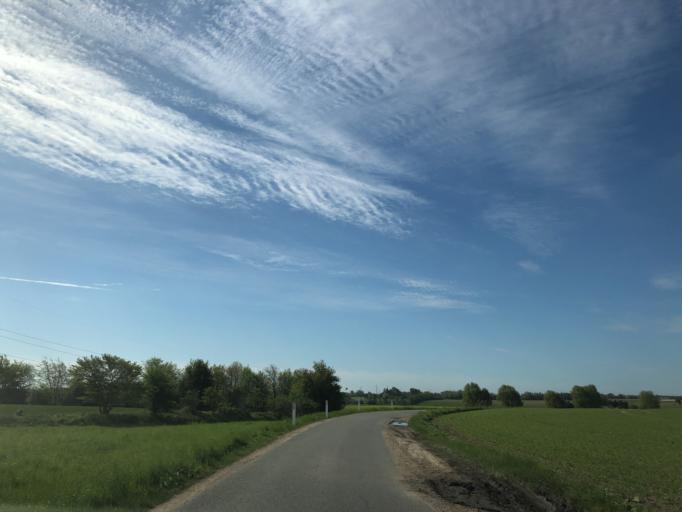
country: DK
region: Zealand
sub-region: Slagelse Kommune
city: Forlev
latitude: 55.3853
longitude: 11.2876
